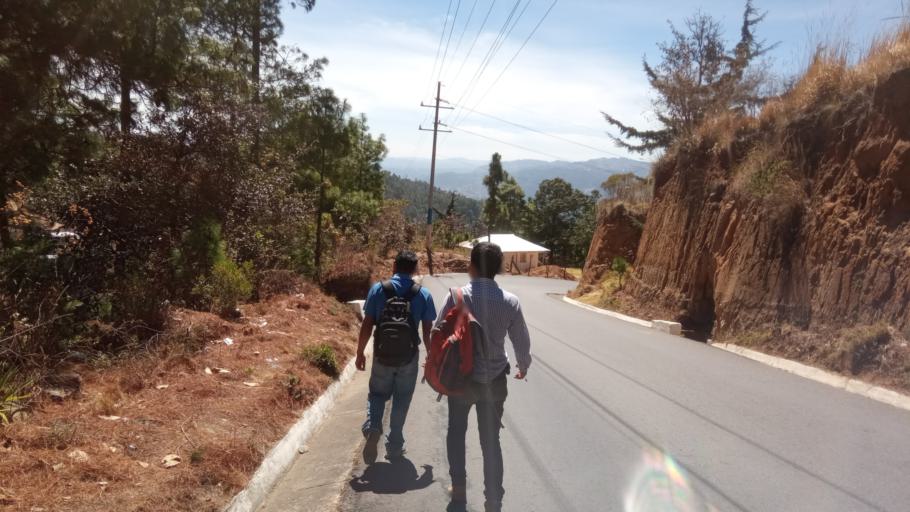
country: GT
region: San Marcos
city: Tejutla
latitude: 15.1383
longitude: -91.7947
